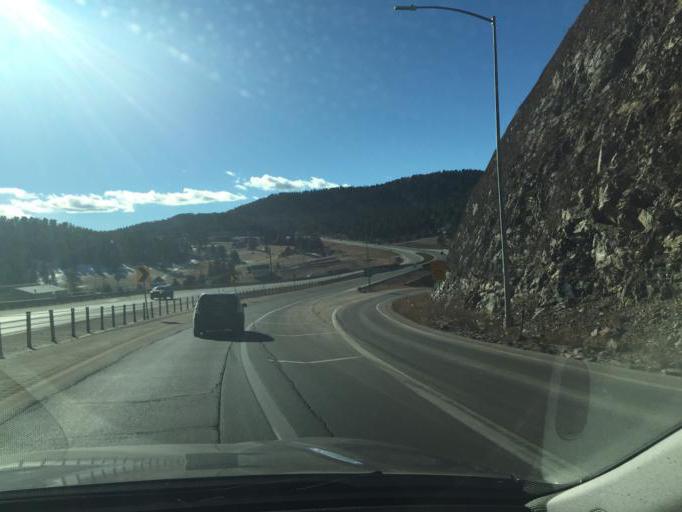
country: US
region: Colorado
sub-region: Jefferson County
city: Evergreen
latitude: 39.4809
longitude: -105.3658
